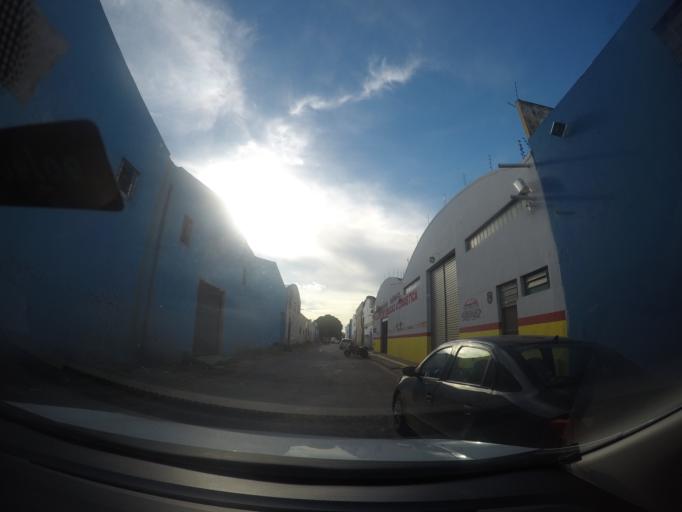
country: BR
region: Goias
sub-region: Goiania
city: Goiania
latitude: -16.6687
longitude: -49.3054
